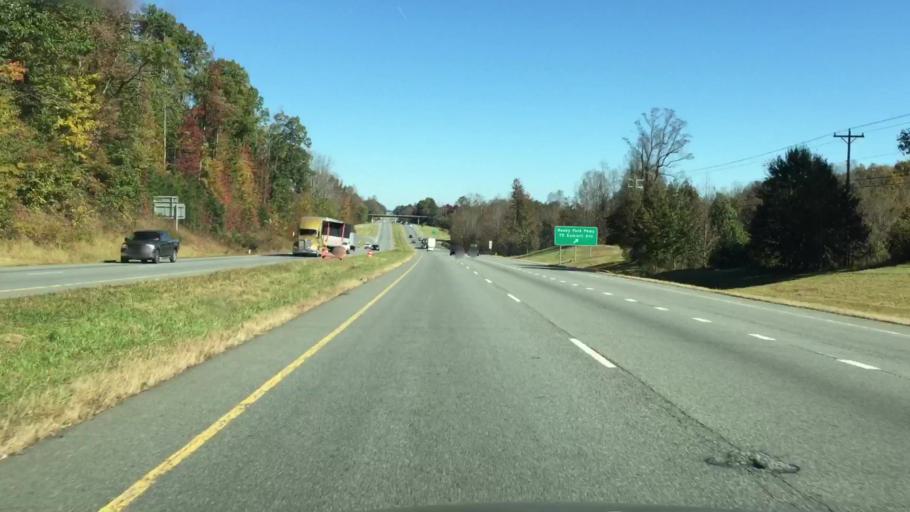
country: US
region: North Carolina
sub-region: Guilford County
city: McLeansville
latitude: 36.1698
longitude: -79.7158
